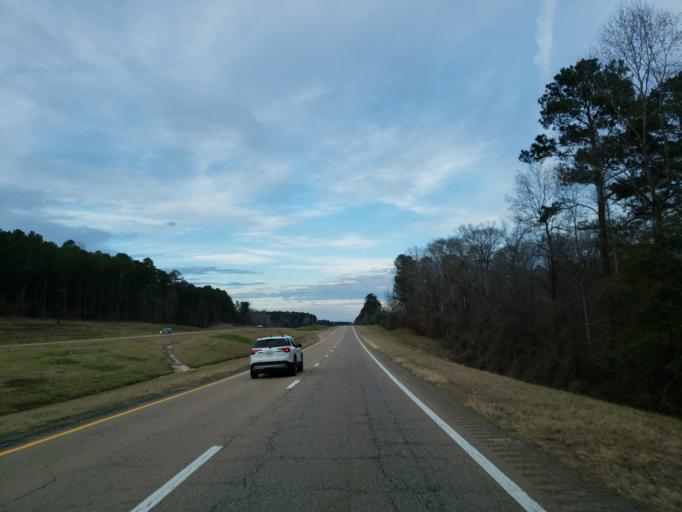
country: US
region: Mississippi
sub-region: Lauderdale County
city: Meridian Station
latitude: 32.4776
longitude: -88.6014
